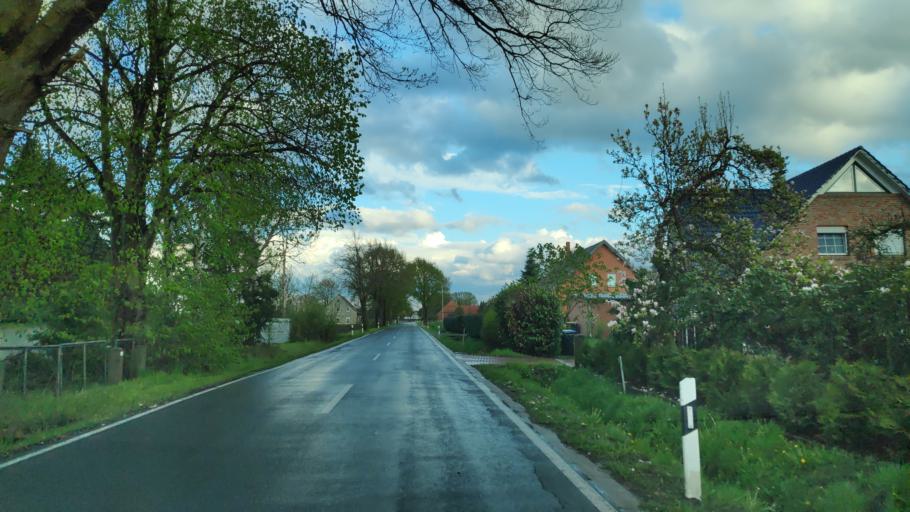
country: DE
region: North Rhine-Westphalia
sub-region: Regierungsbezirk Detmold
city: Hille
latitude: 52.3555
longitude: 8.8149
